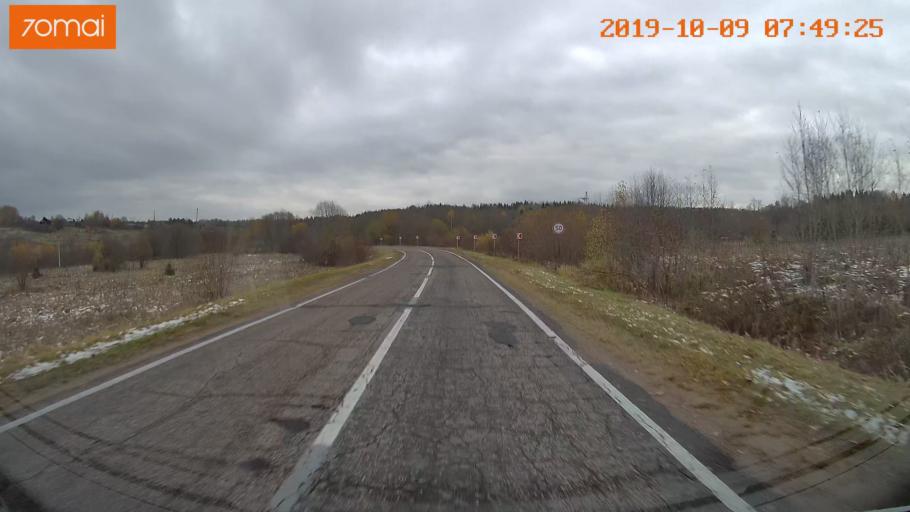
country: RU
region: Jaroslavl
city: Kukoboy
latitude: 58.6673
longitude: 39.8469
